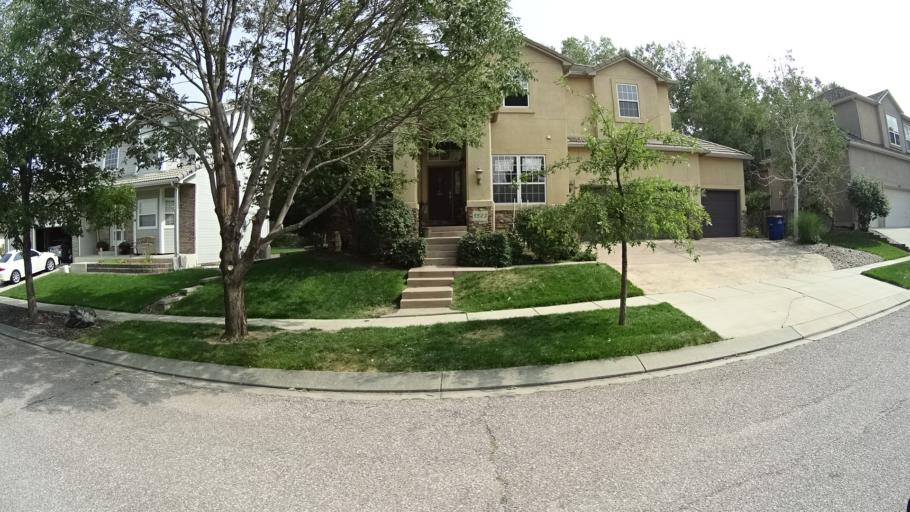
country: US
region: Colorado
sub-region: El Paso County
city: Cimarron Hills
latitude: 38.9169
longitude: -104.7423
